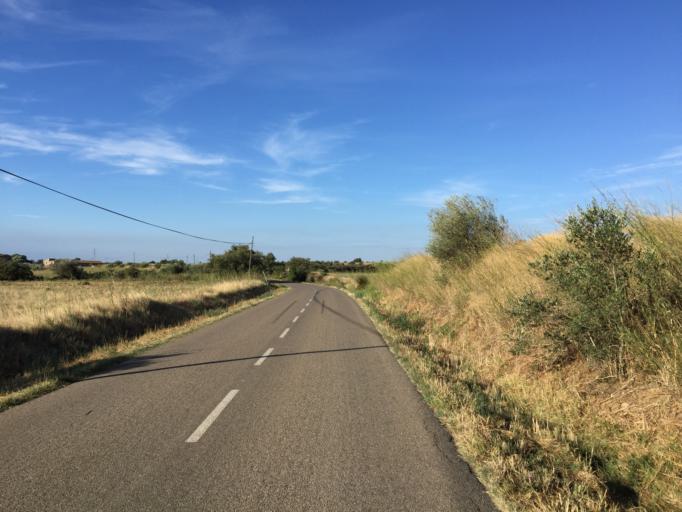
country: ES
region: Catalonia
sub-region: Provincia de Girona
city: Vilajuiga
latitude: 42.2986
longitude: 3.0792
